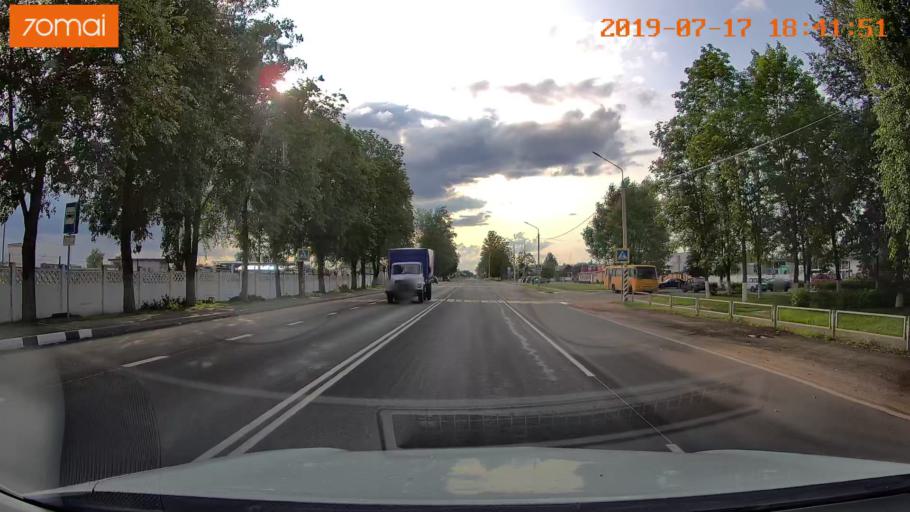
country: BY
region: Mogilev
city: Asipovichy
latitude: 53.3076
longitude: 28.6561
